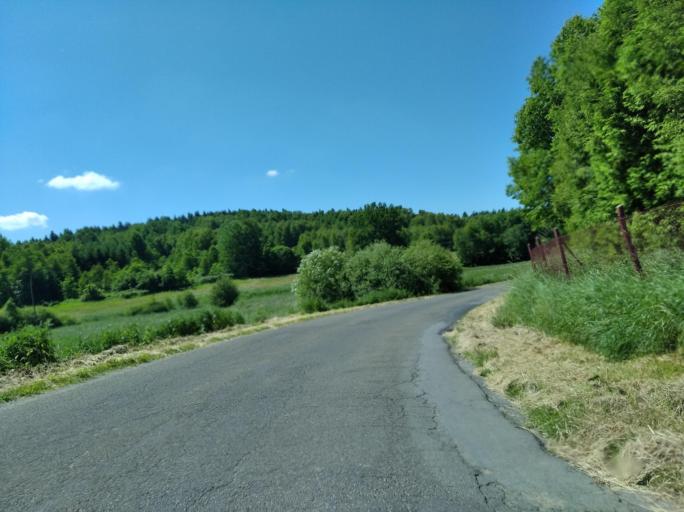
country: PL
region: Subcarpathian Voivodeship
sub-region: Powiat krosnienski
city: Chorkowka
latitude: 49.6416
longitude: 21.6361
